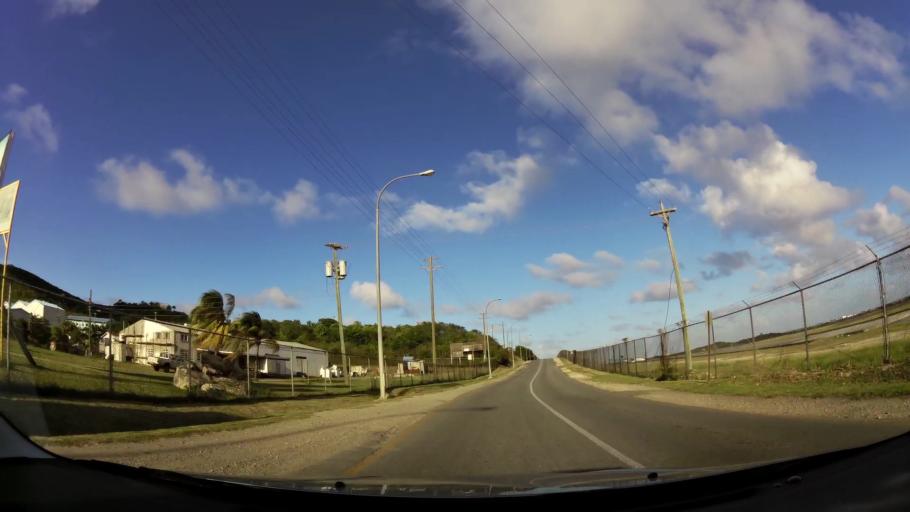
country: AG
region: Saint George
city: Piggotts
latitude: 17.1334
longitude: -61.8016
